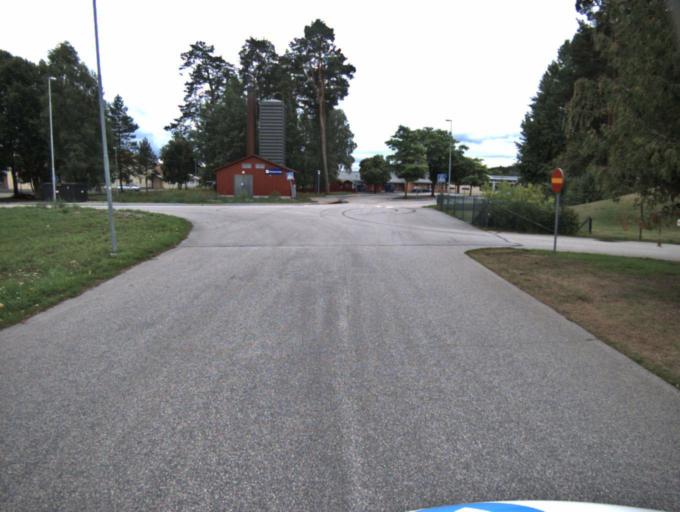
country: SE
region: Vaestra Goetaland
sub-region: Ulricehamns Kommun
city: Ulricehamn
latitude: 57.8583
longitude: 13.4280
